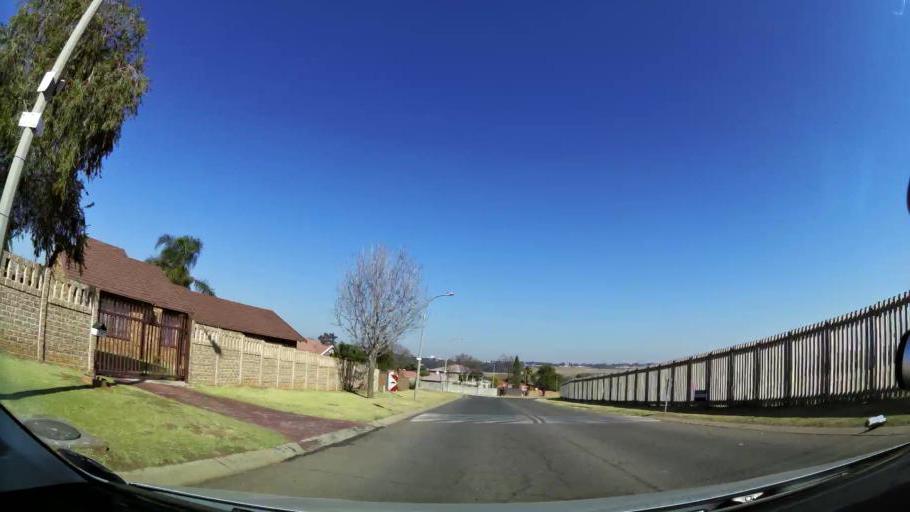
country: ZA
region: Gauteng
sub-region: City of Johannesburg Metropolitan Municipality
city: Modderfontein
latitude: -26.0552
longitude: 28.2018
